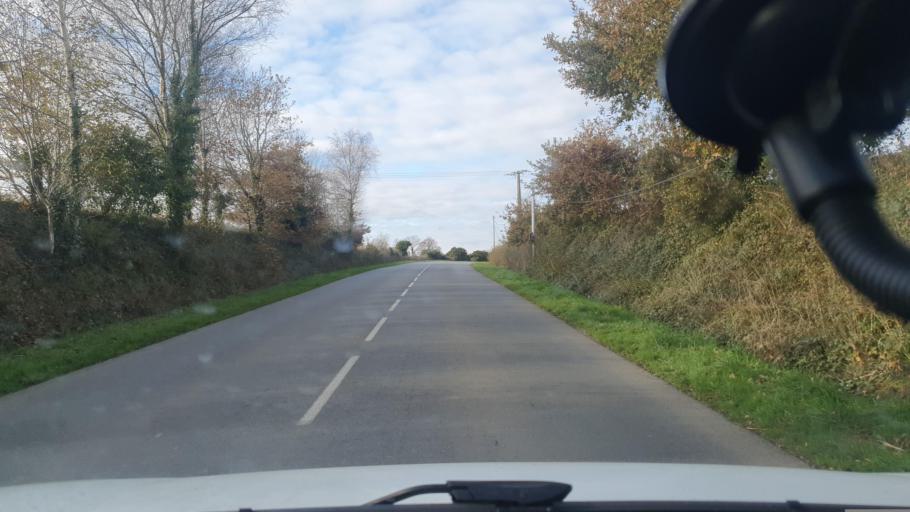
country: FR
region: Brittany
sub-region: Departement du Finistere
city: Edern
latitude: 48.0912
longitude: -3.9806
